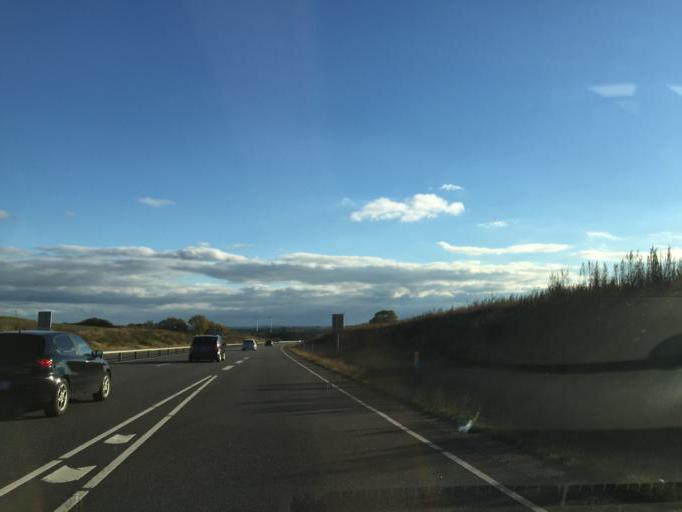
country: DK
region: Zealand
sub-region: Odsherred Kommune
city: Asnaes
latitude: 55.7891
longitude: 11.5835
